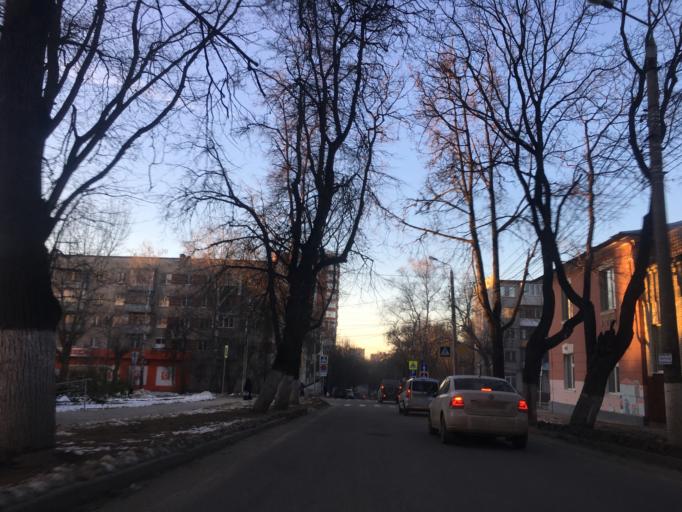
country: RU
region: Tula
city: Tula
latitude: 54.1862
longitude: 37.6006
